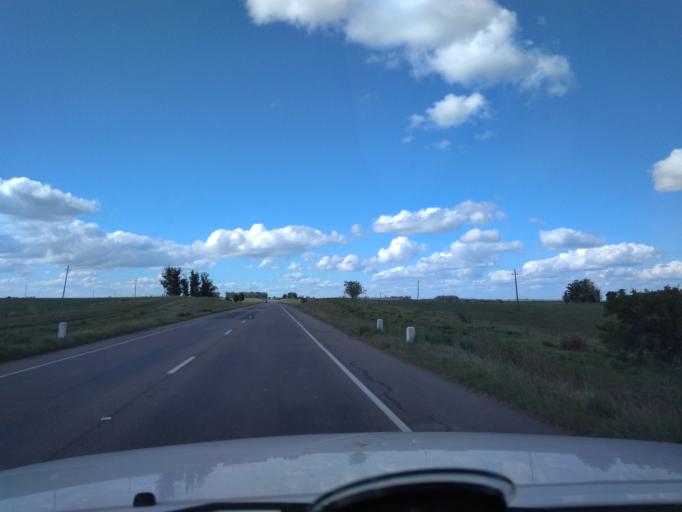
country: UY
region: Florida
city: Cardal
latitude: -34.3135
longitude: -56.2392
